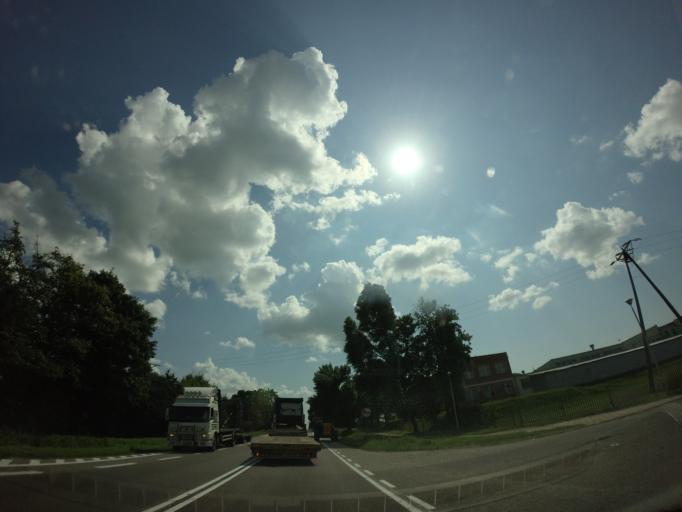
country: PL
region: Podlasie
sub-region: Powiat lomzynski
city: Piatnica
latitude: 53.2116
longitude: 22.1044
